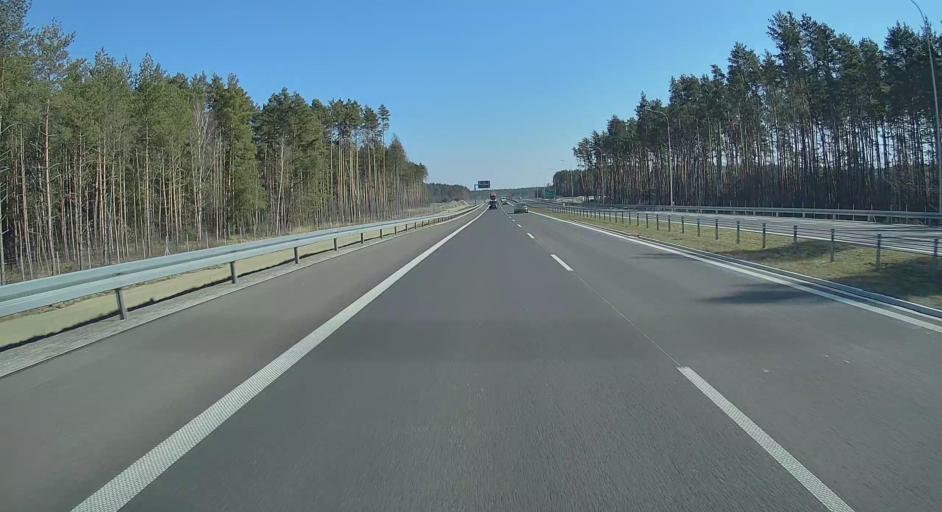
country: PL
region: Subcarpathian Voivodeship
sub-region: Powiat nizanski
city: Raclawice
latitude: 50.4731
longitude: 22.1583
